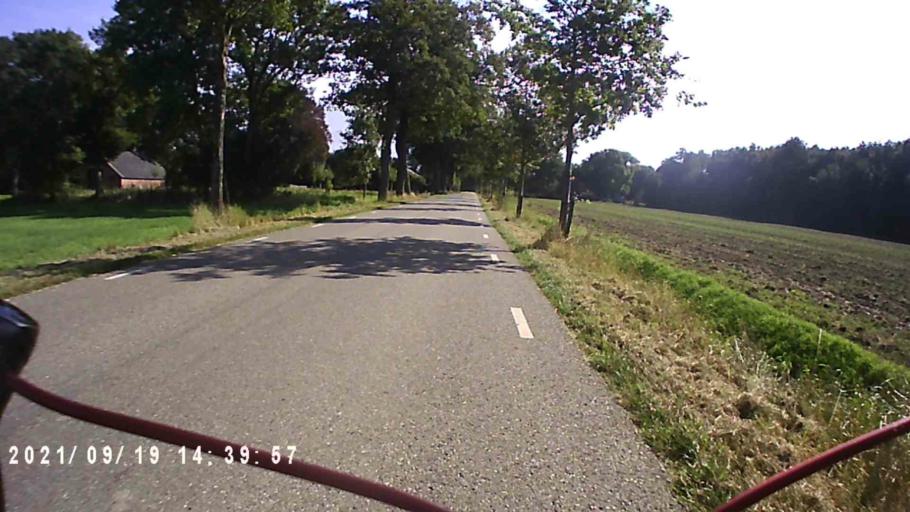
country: DE
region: Lower Saxony
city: Bunde
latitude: 53.1299
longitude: 7.1681
